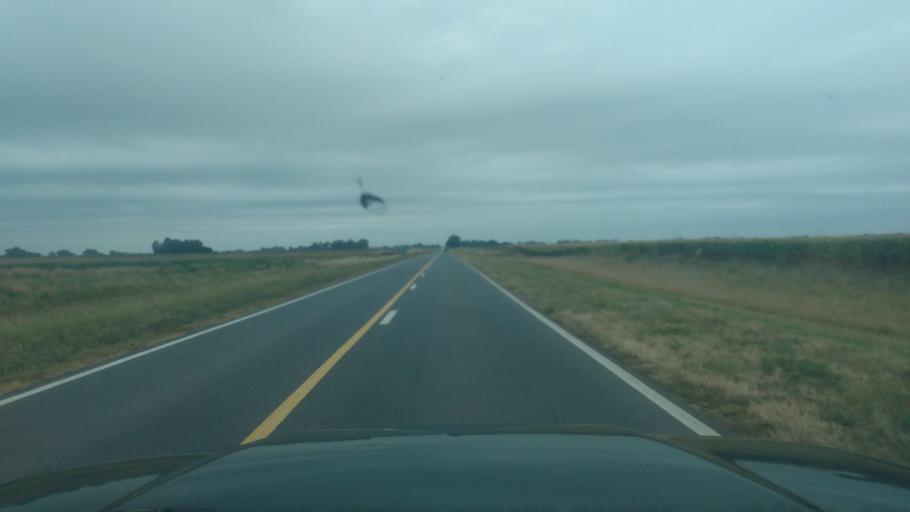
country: AR
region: Buenos Aires
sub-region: Partido de Bragado
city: Bragado
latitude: -35.3119
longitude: -60.6276
